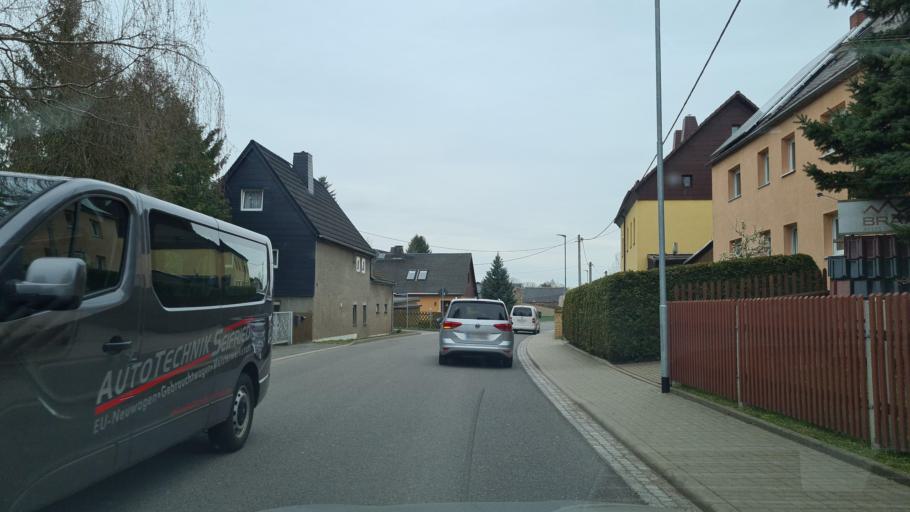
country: DE
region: Saxony
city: Hilbersdorf
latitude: 50.9039
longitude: 12.9337
